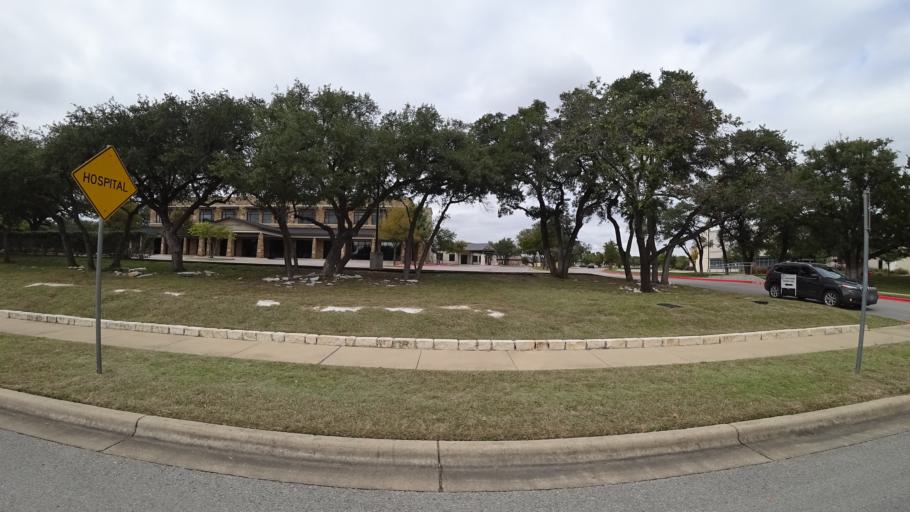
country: US
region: Texas
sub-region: Williamson County
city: Brushy Creek
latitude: 30.5120
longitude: -97.7138
